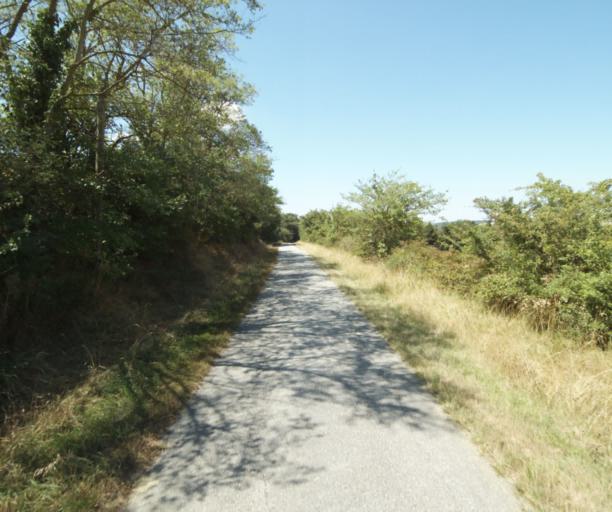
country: FR
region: Midi-Pyrenees
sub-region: Departement de la Haute-Garonne
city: Saint-Felix-Lauragais
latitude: 43.4627
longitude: 1.8905
